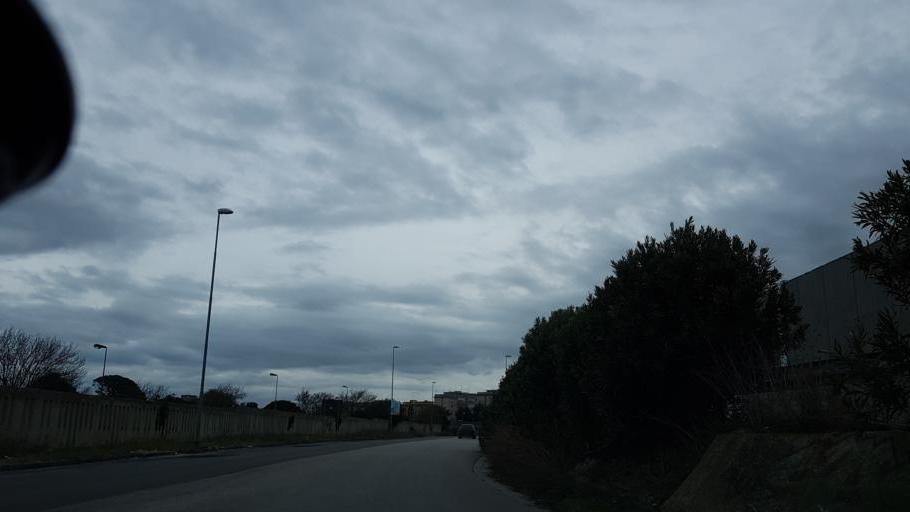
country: IT
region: Apulia
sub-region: Provincia di Brindisi
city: Brindisi
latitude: 40.6241
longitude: 17.9101
